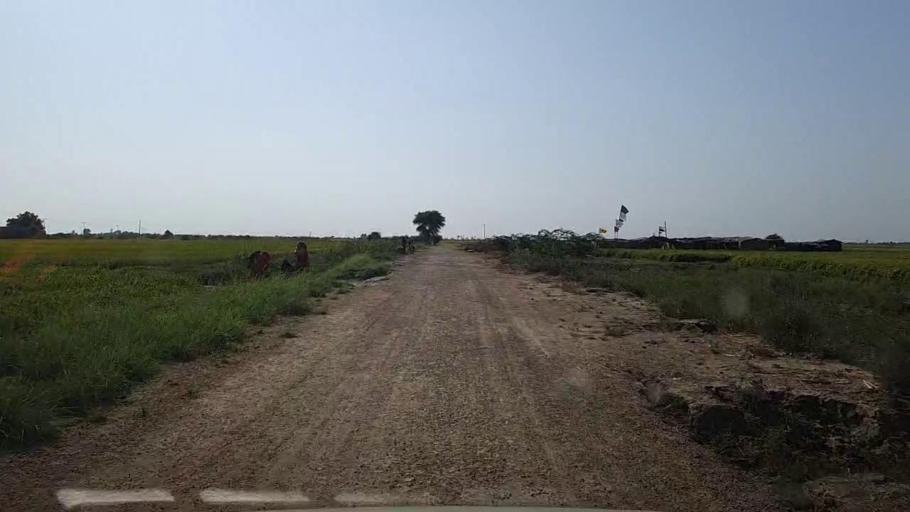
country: PK
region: Sindh
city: Kario
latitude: 24.8296
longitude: 68.5262
